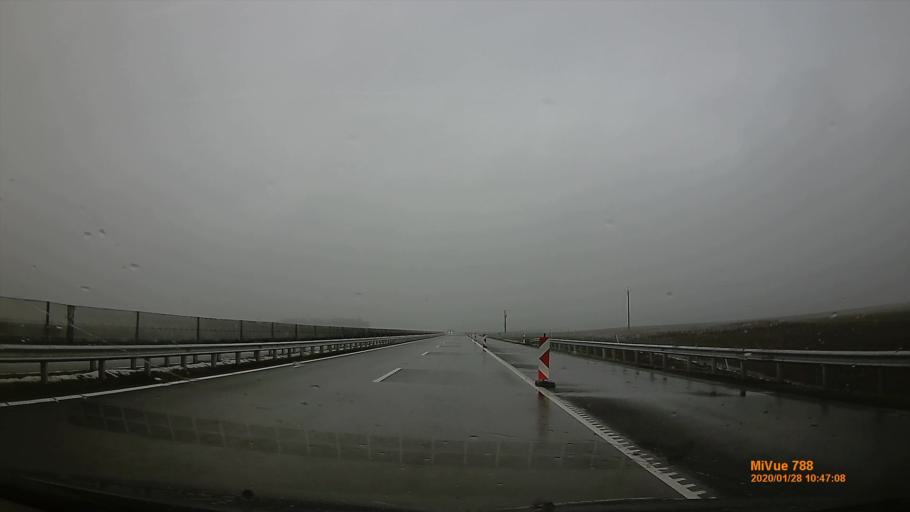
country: HU
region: Pest
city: Monor
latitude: 47.3715
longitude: 19.4757
